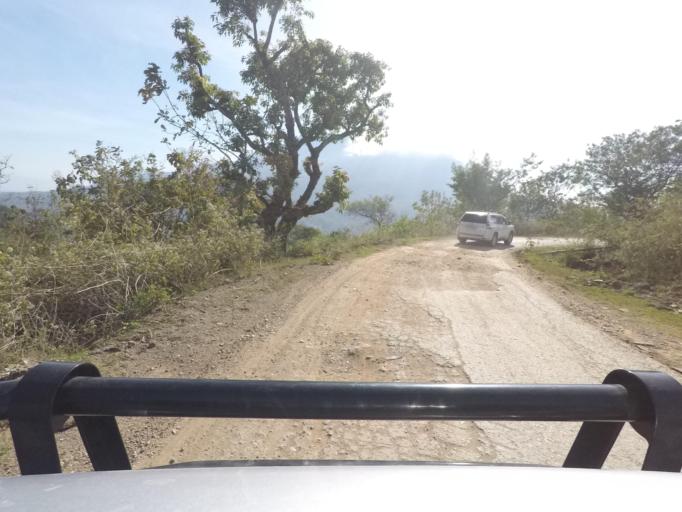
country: TL
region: Bobonaro
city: Maliana
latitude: -9.0080
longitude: 125.2469
